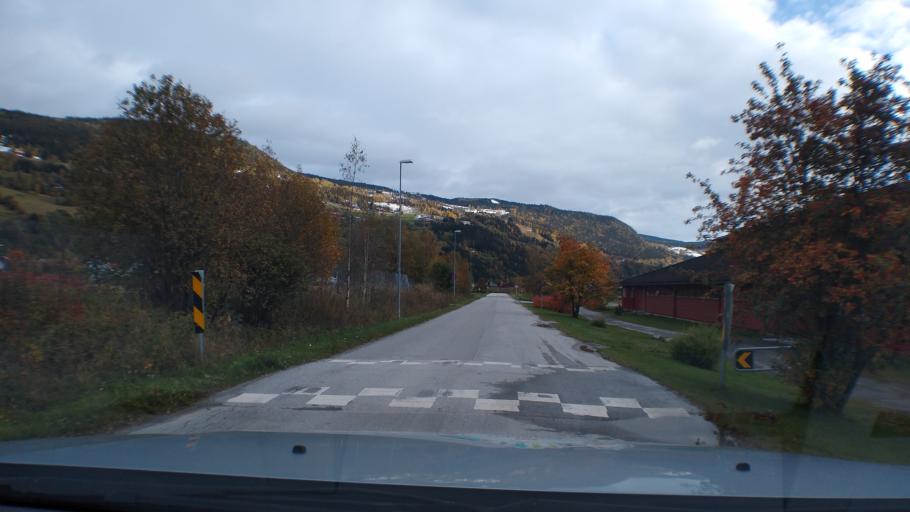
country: NO
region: Oppland
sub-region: Ringebu
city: Ringebu
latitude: 61.5254
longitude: 10.1442
